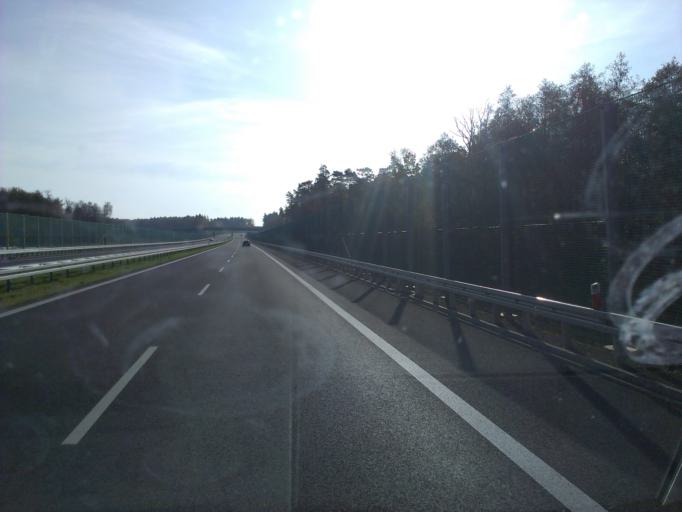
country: PL
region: Lubusz
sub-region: Powiat miedzyrzecki
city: Miedzyrzecz
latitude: 52.5133
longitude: 15.5496
